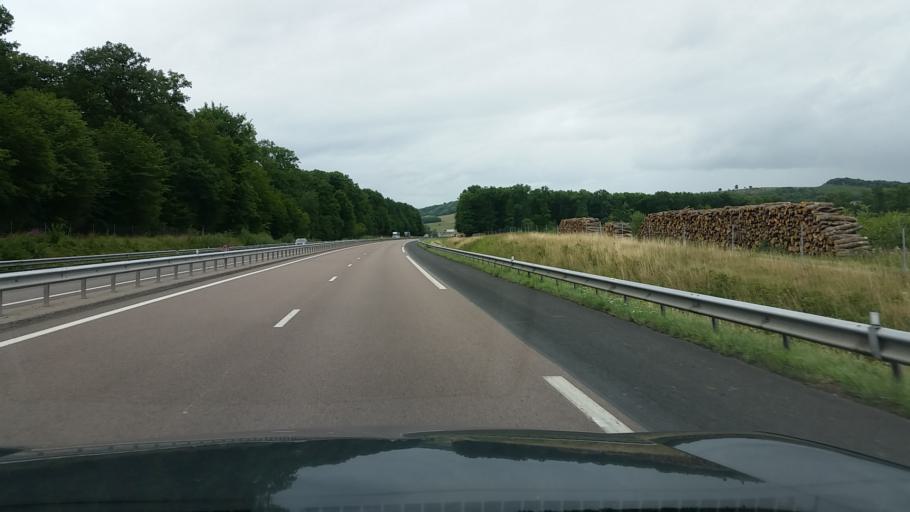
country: FR
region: Lorraine
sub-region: Departement des Vosges
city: Chatenois
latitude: 48.3155
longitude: 5.8546
